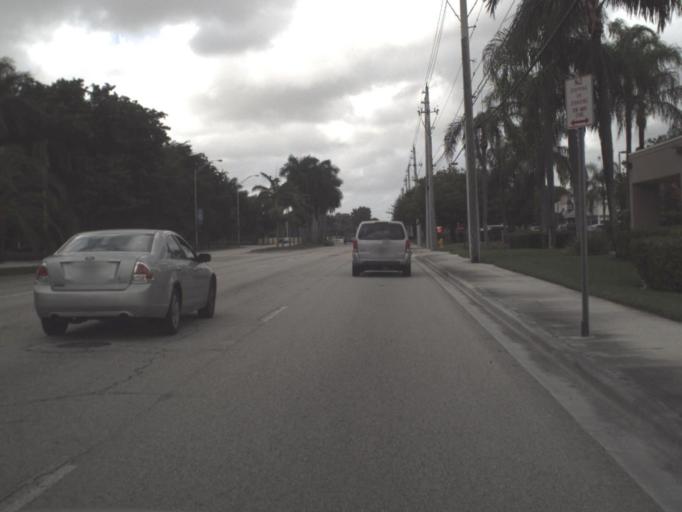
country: US
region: Florida
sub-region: Miami-Dade County
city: Doral
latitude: 25.8118
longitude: -80.3553
